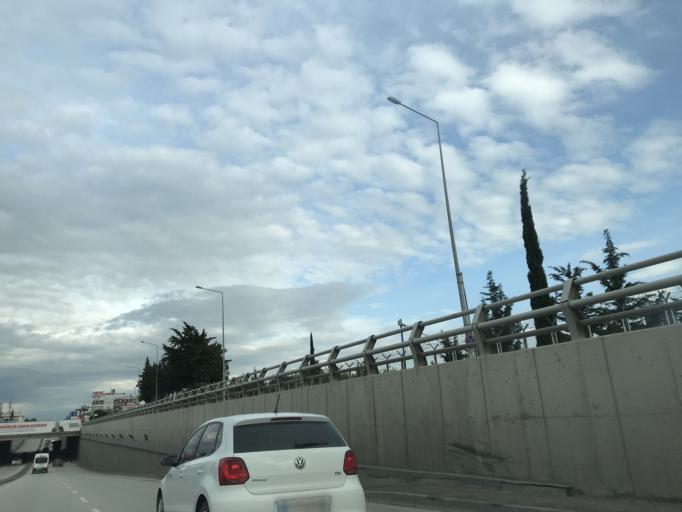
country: TR
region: Adana
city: Seyhan
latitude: 36.9935
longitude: 35.2977
